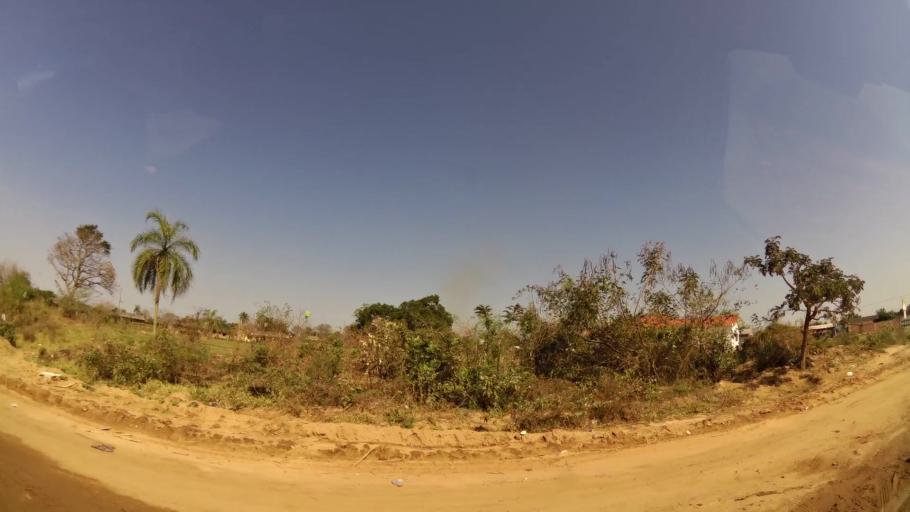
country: BO
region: Santa Cruz
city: Cotoca
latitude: -17.7114
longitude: -63.0639
